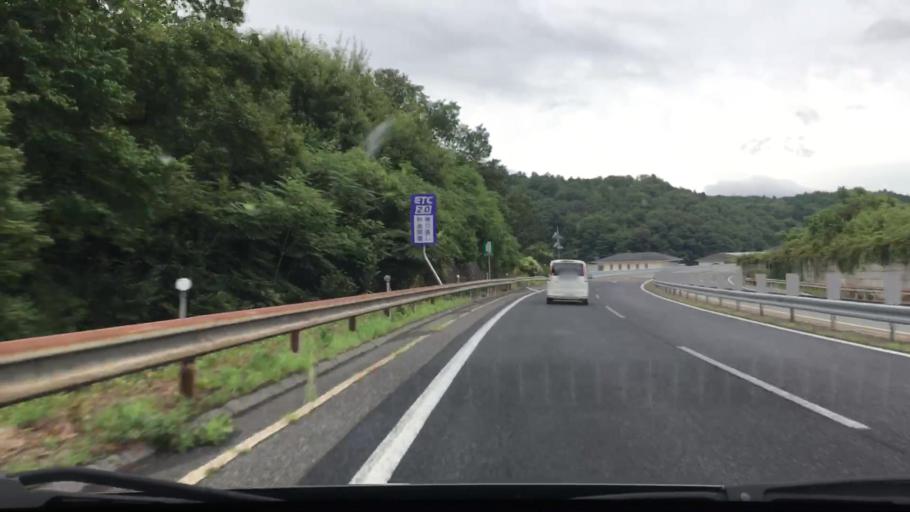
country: JP
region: Hiroshima
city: Hiroshima-shi
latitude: 34.6782
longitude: 132.5603
